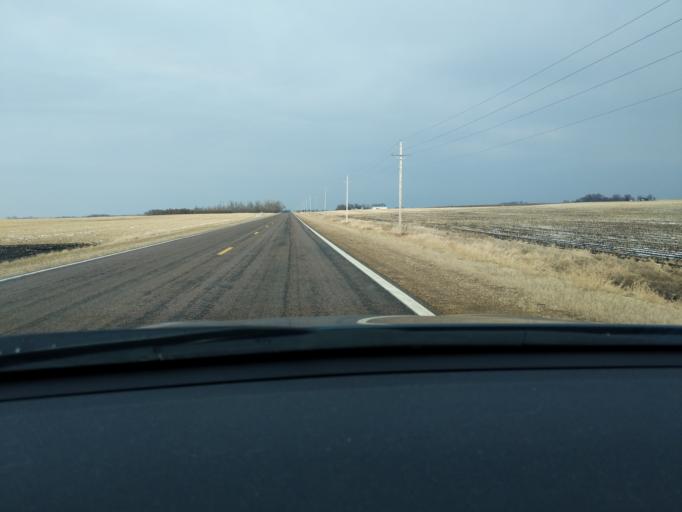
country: US
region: Minnesota
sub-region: Renville County
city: Renville
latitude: 44.7472
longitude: -95.3407
